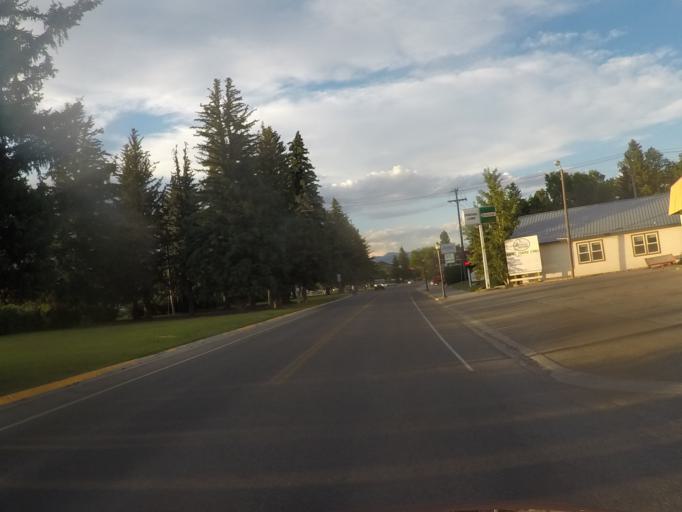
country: US
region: Montana
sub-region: Park County
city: Livingston
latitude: 45.6566
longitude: -110.5694
